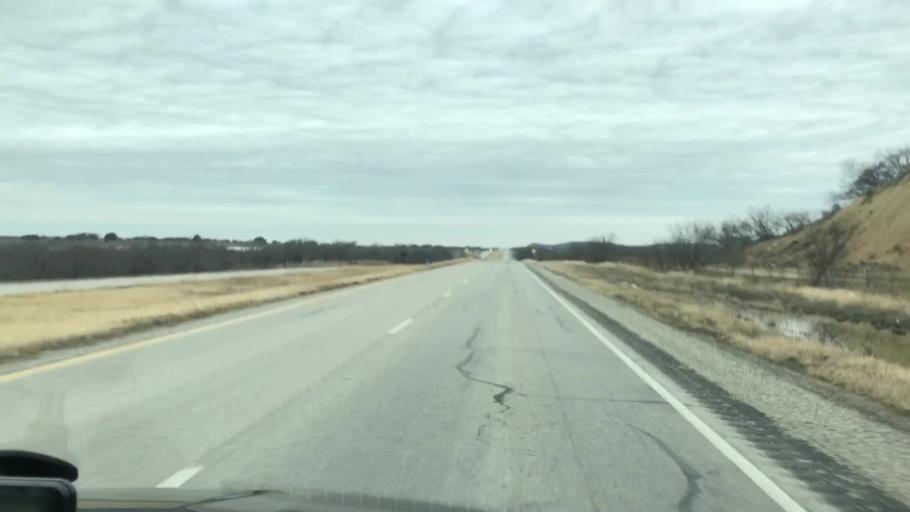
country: US
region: Texas
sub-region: Jack County
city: Jacksboro
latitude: 33.2384
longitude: -98.2125
